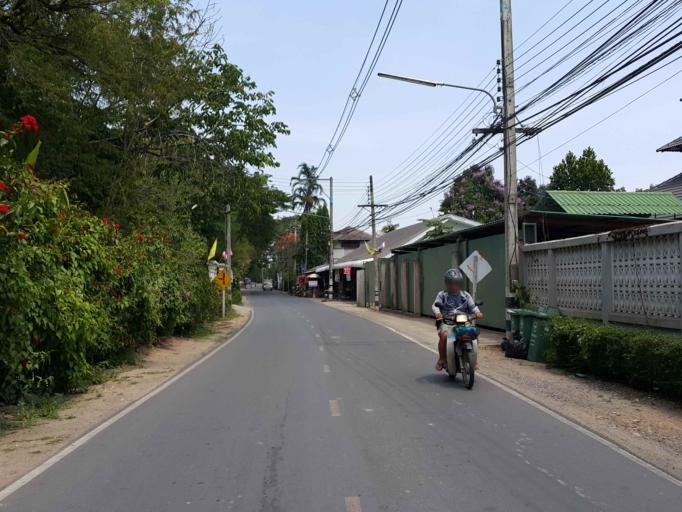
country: TH
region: Chiang Mai
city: Chiang Mai
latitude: 18.8327
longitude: 98.9941
